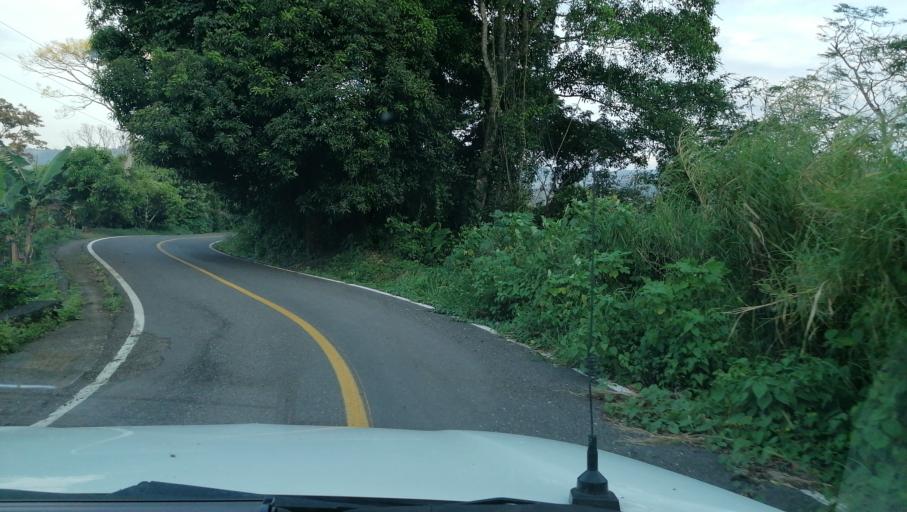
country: MX
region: Chiapas
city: Pichucalco
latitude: 17.5061
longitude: -93.2154
